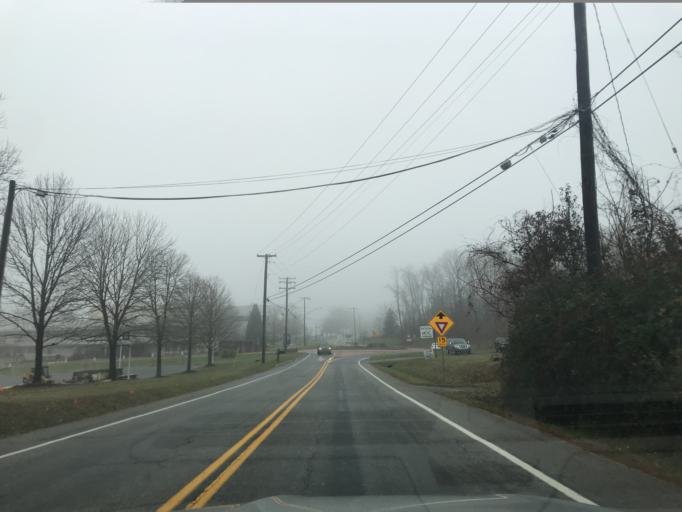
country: US
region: Maryland
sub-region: Harford County
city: South Bel Air
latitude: 39.5627
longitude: -76.2873
